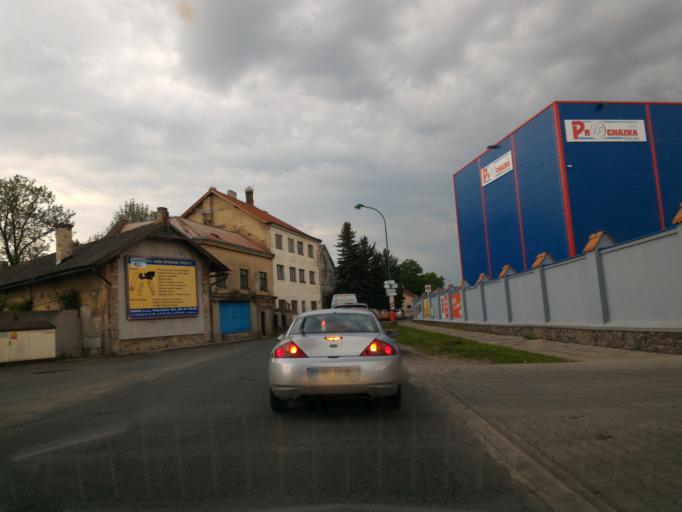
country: CZ
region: Central Bohemia
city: Velim
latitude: 50.0685
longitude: 15.1293
